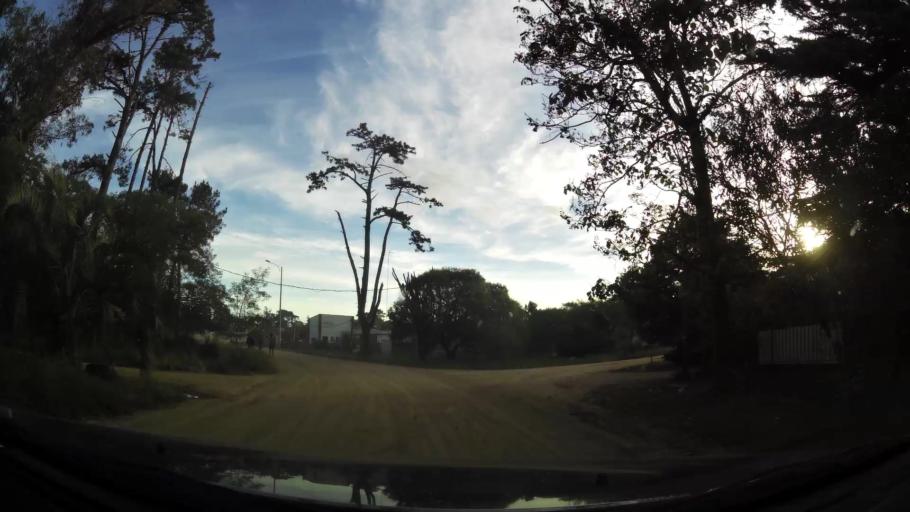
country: UY
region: Canelones
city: Atlantida
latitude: -34.7701
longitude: -55.8197
